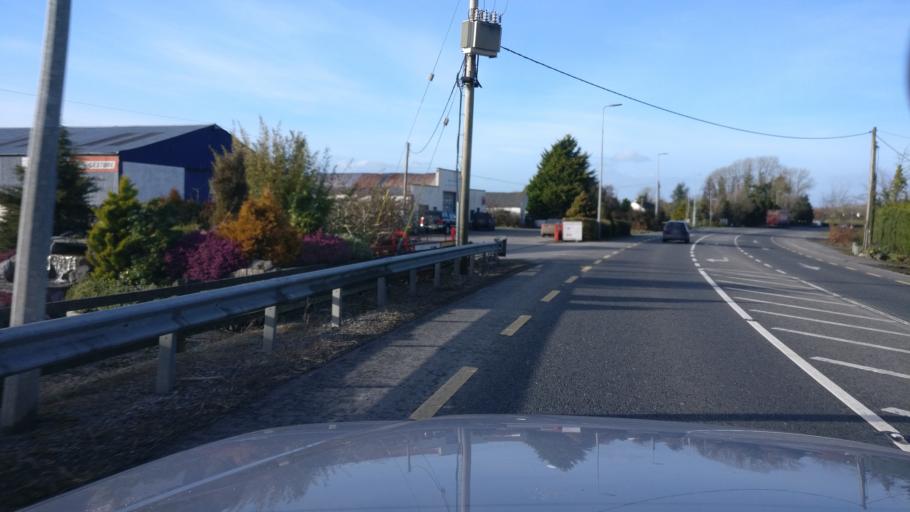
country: IE
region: Leinster
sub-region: Uibh Fhaili
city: Tullamore
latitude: 53.2204
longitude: -7.4744
